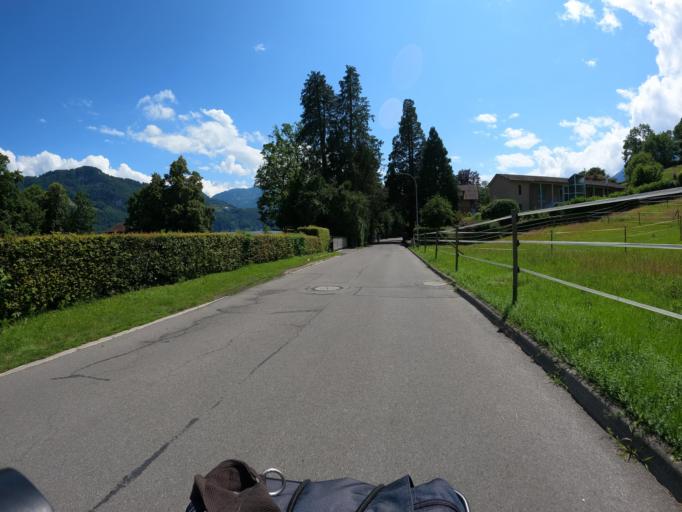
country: CH
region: Nidwalden
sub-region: Nidwalden
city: Stansstad
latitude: 47.0059
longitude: 8.3393
